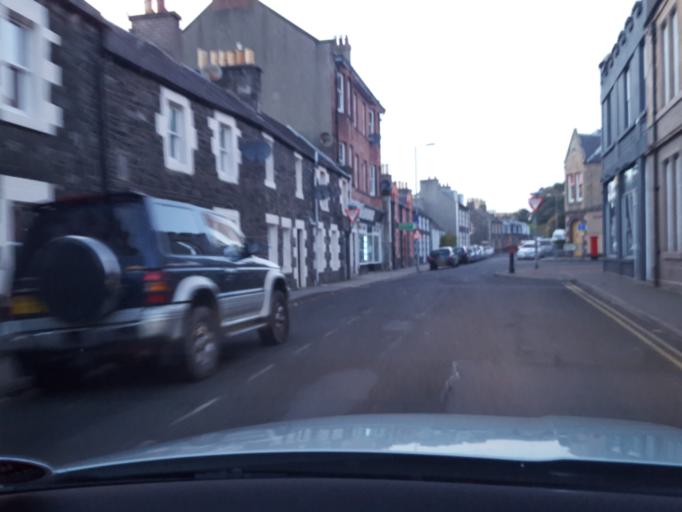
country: GB
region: Scotland
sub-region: The Scottish Borders
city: Peebles
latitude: 55.6540
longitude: -3.1891
